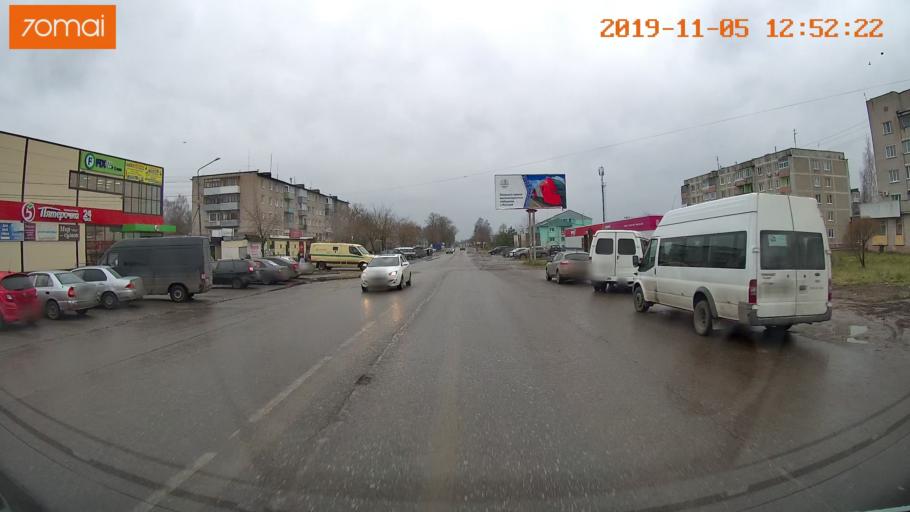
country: RU
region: Ivanovo
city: Kokhma
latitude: 56.9402
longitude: 41.1077
